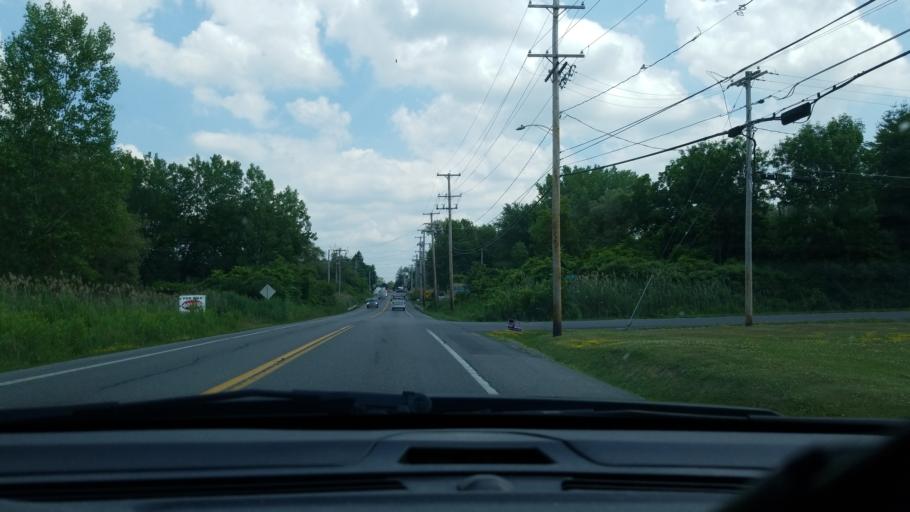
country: US
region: New York
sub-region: Onondaga County
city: Liverpool
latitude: 43.1509
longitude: -76.1932
